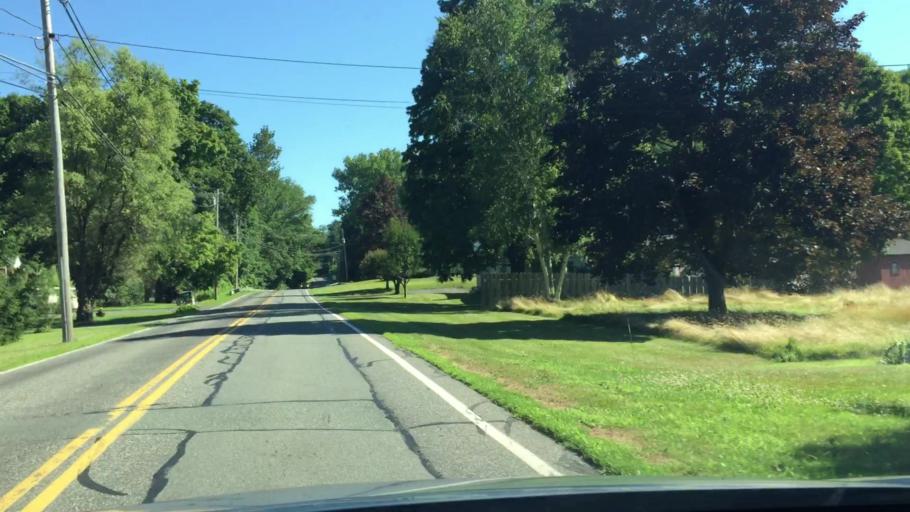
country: US
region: Massachusetts
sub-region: Berkshire County
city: West Stockbridge
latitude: 42.3398
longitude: -73.3669
